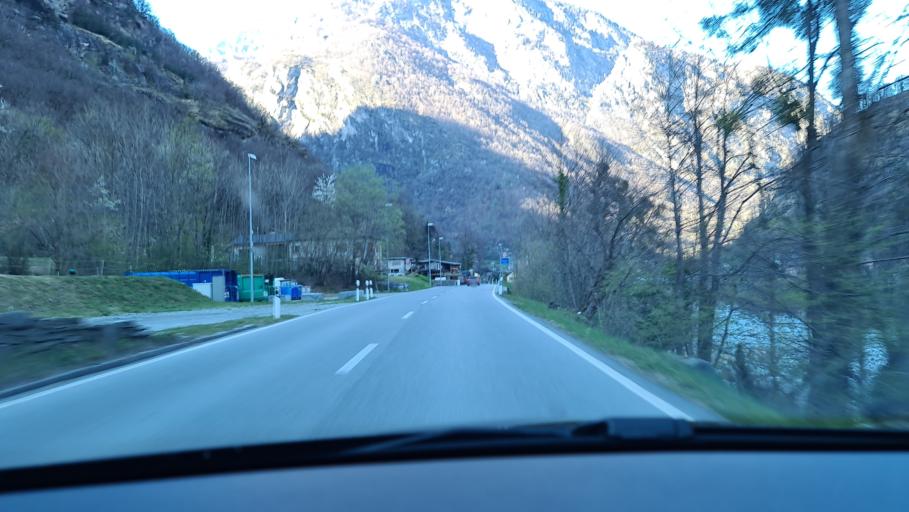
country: CH
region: Ticino
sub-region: Vallemaggia District
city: Cevio
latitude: 46.3349
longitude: 8.6063
